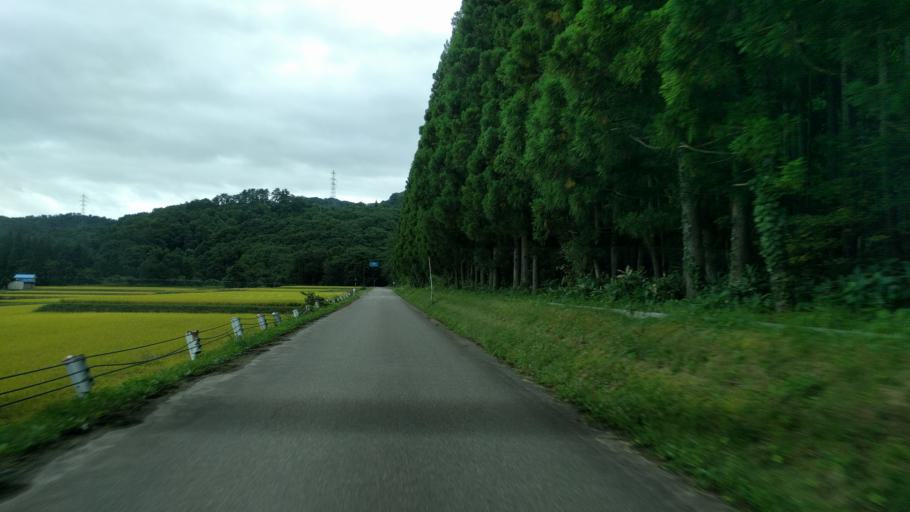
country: JP
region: Fukushima
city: Kitakata
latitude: 37.5405
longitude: 139.7411
